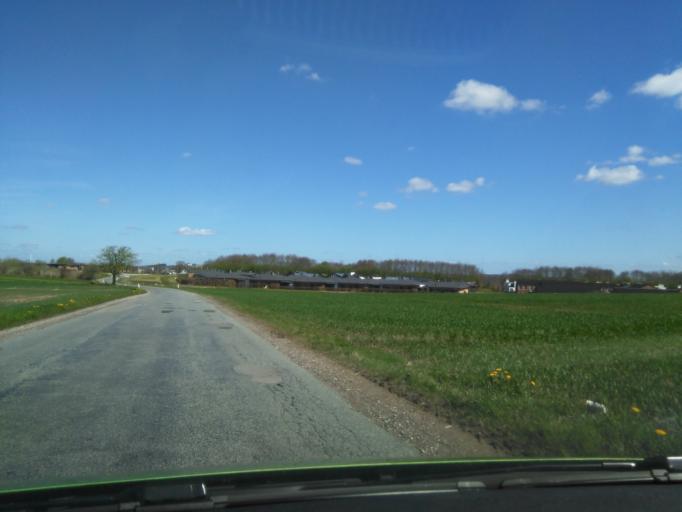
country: DK
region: Central Jutland
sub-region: Arhus Kommune
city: Marslet
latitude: 56.0587
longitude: 10.1550
